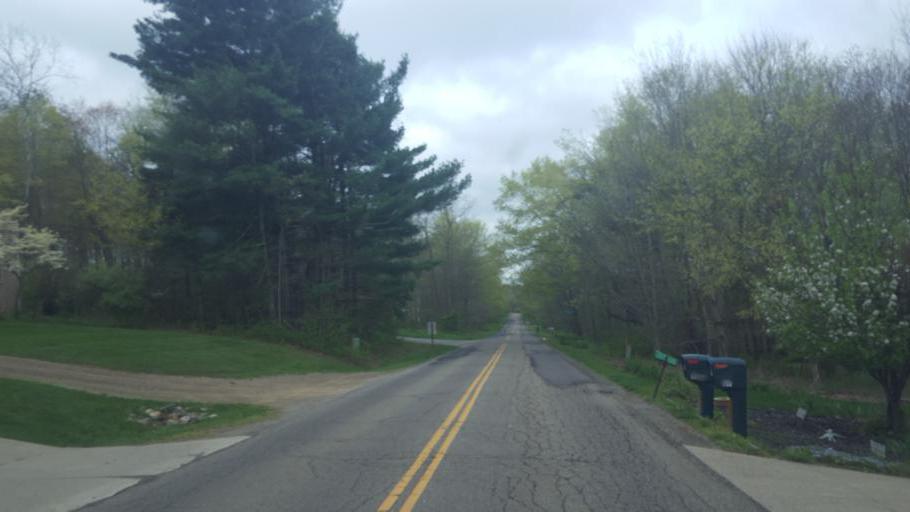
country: US
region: Ohio
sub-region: Knox County
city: Gambier
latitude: 40.4163
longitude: -82.3573
